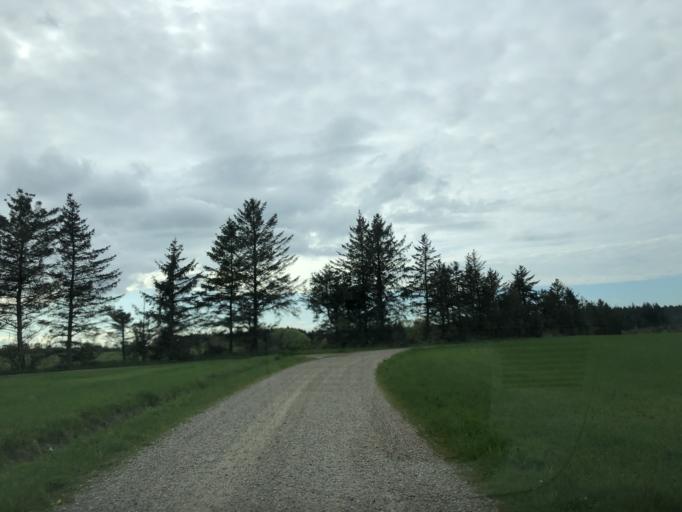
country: DK
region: Central Jutland
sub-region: Holstebro Kommune
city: Ulfborg
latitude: 56.1986
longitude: 8.4378
